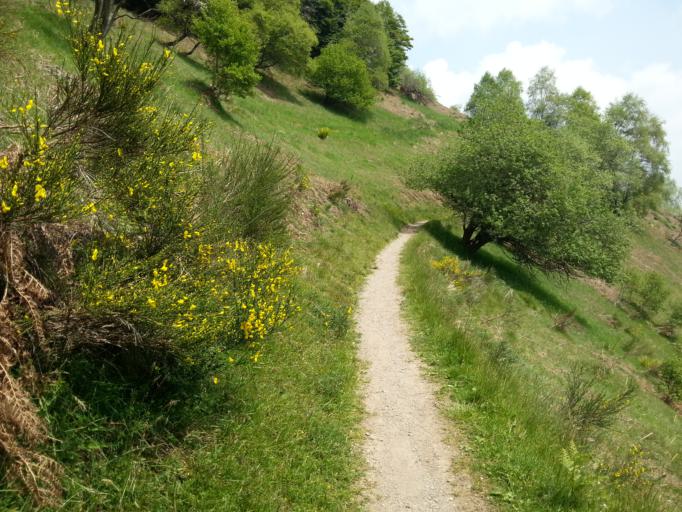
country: CH
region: Ticino
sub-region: Lugano District
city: Melano
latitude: 45.9157
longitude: 9.0071
